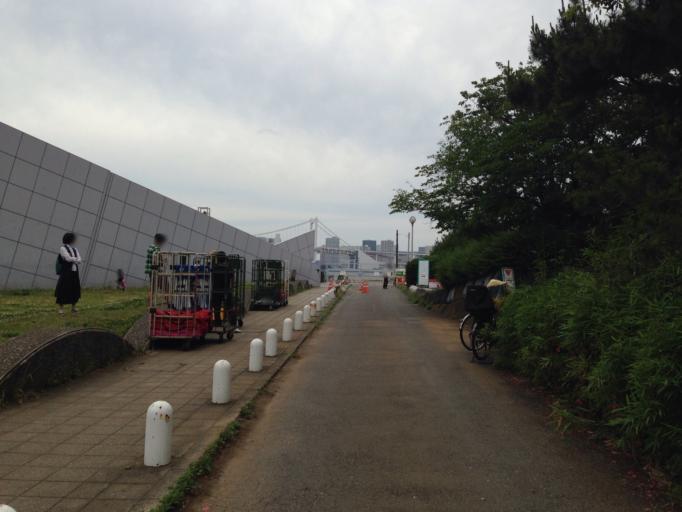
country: JP
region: Tokyo
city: Tokyo
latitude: 35.6473
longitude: 139.7726
